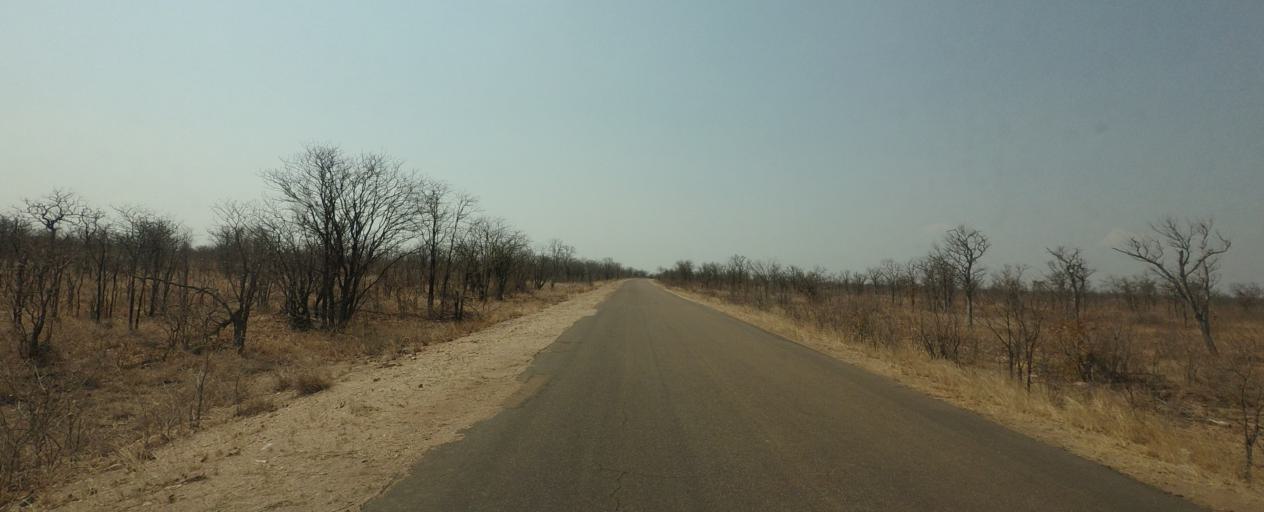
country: ZA
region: Limpopo
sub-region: Mopani District Municipality
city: Giyani
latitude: -23.3551
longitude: 31.3189
